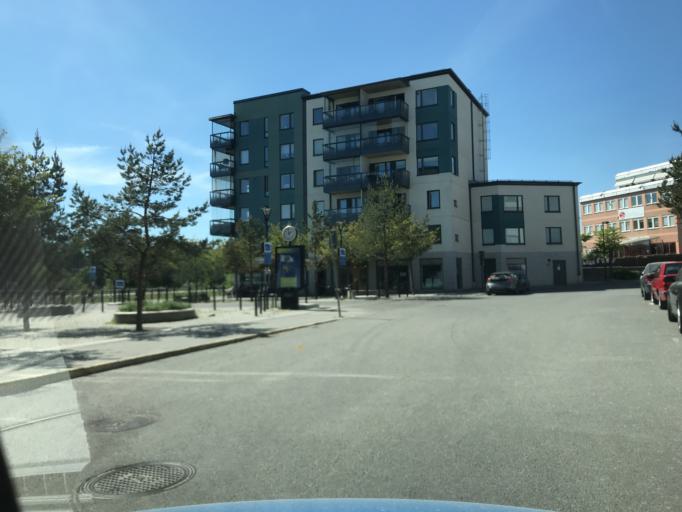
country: SE
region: Stockholm
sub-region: Solna Kommun
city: Rasunda
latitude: 59.4030
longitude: 17.9815
